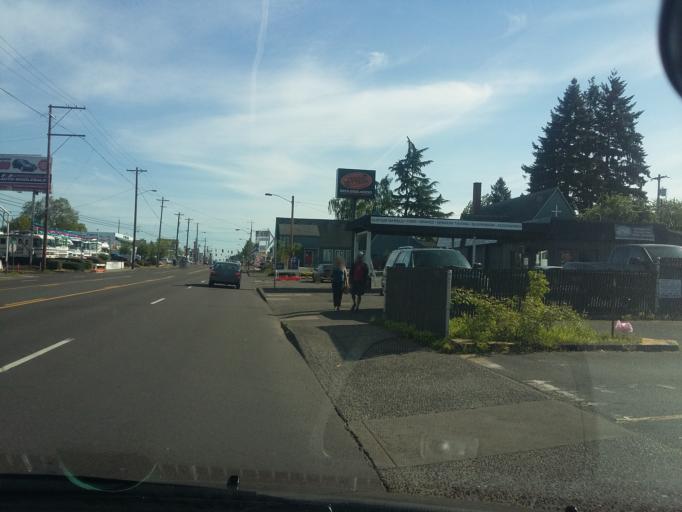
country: US
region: Oregon
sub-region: Multnomah County
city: Lents
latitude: 45.5217
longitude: -122.5792
